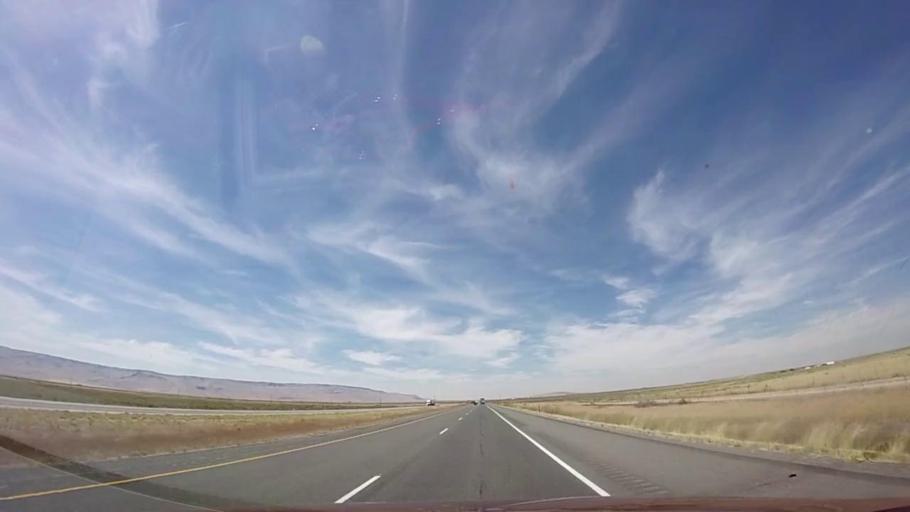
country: US
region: Idaho
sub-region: Minidoka County
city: Rupert
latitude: 42.4315
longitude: -113.3381
